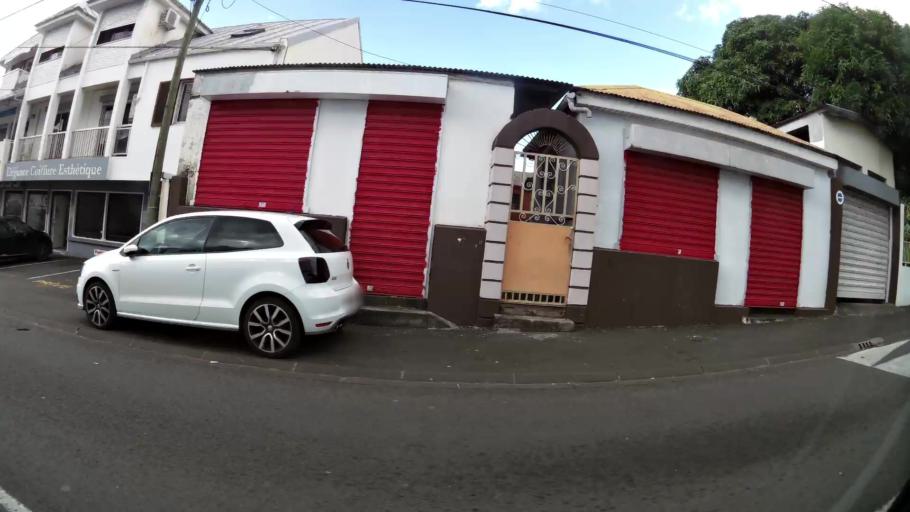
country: RE
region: Reunion
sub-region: Reunion
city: Saint-Denis
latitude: -20.8937
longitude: 55.4818
